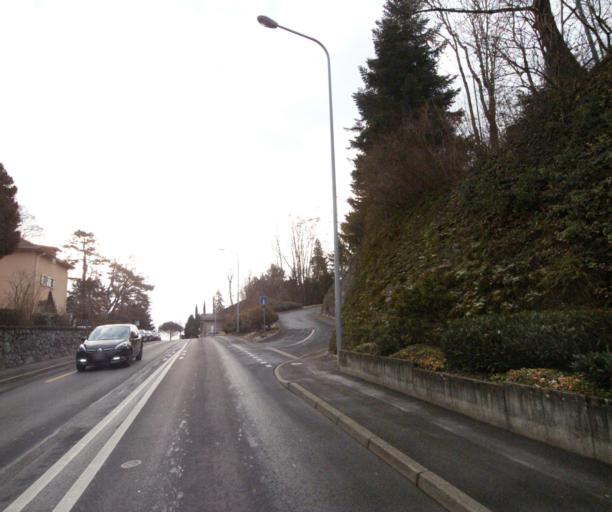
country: CH
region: Vaud
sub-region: Riviera-Pays-d'Enhaut District
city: La Tour-de-Peilz
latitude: 46.4535
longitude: 6.8682
